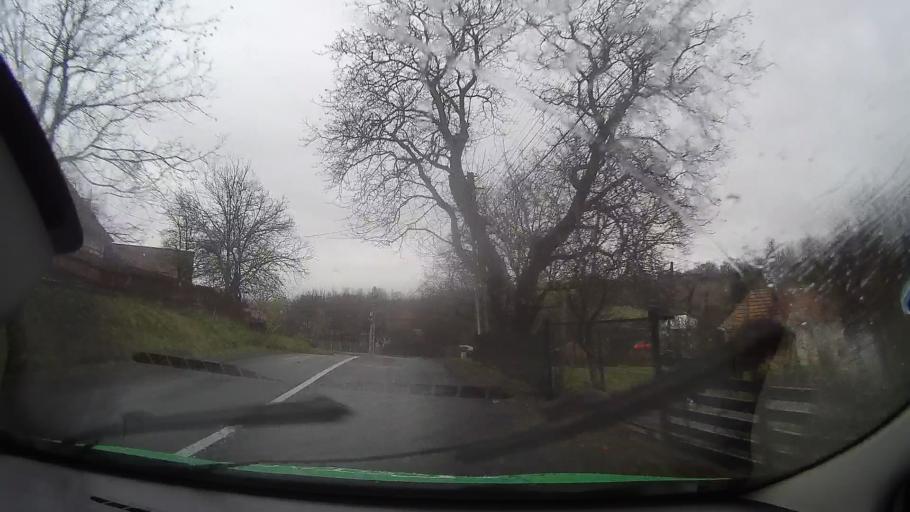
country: RO
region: Mures
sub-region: Comuna Vatava
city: Vatava
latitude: 46.9547
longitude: 24.7630
